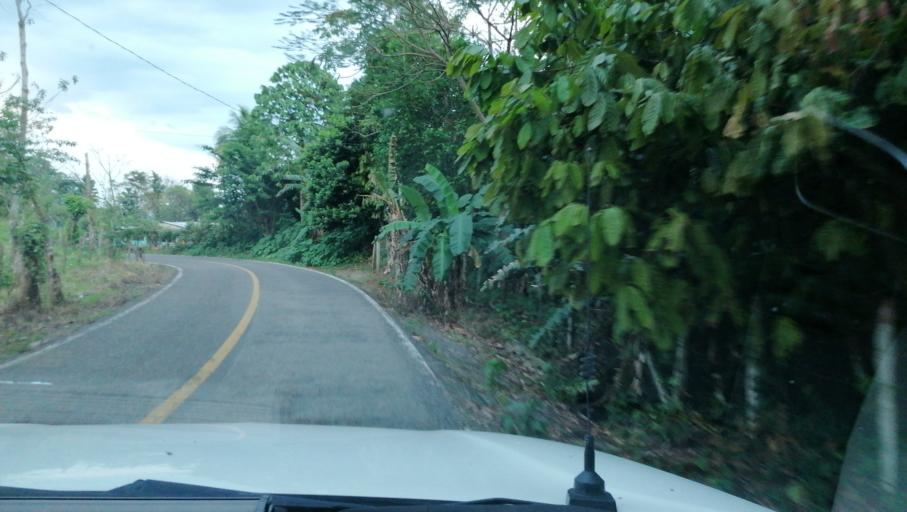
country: MX
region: Chiapas
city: Pichucalco
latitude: 17.5280
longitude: -93.1542
